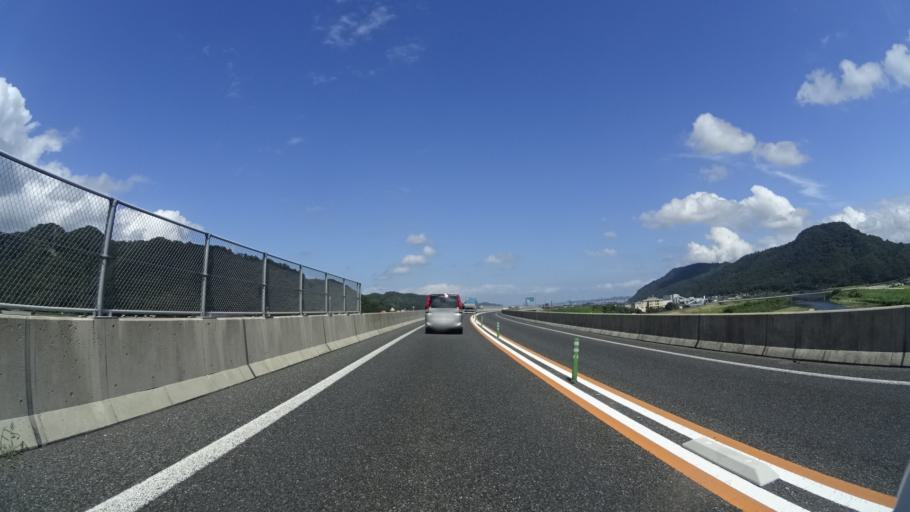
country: JP
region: Tottori
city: Tottori
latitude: 35.4177
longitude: 134.2059
